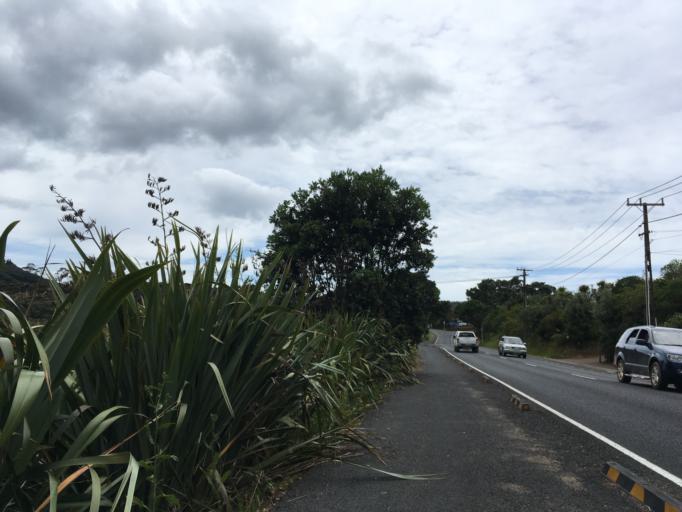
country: NZ
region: Auckland
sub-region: Auckland
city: Pakuranga
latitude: -36.7967
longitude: 175.0426
